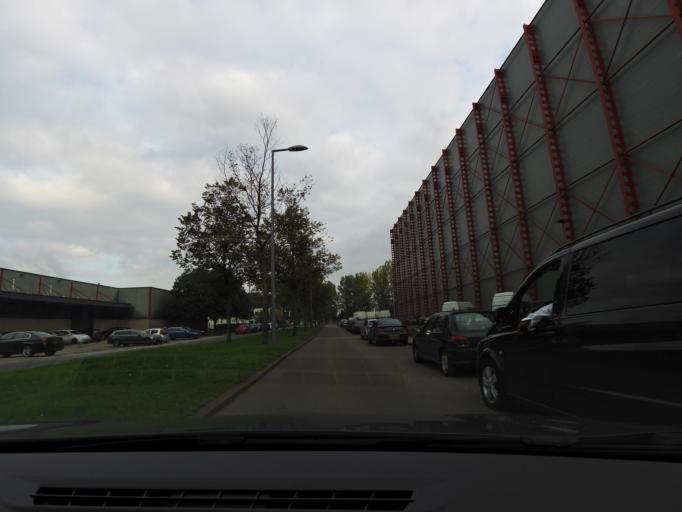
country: NL
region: South Holland
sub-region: Gemeente Schiedam
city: Schiedam
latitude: 51.9400
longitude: 4.4116
